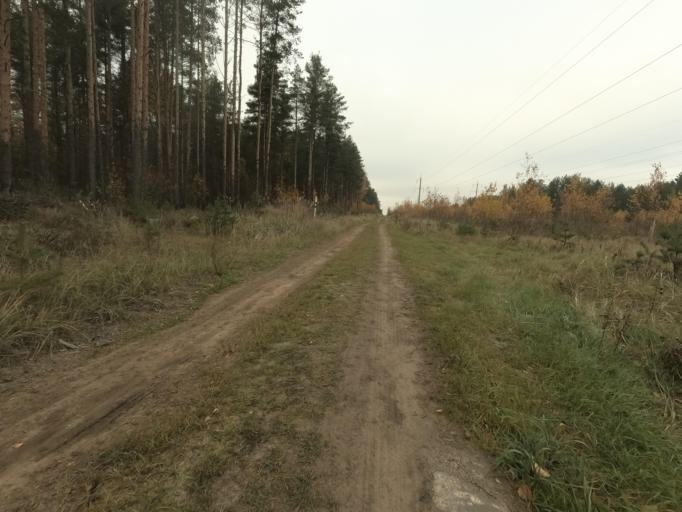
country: RU
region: Leningrad
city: Kirovsk
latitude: 59.8496
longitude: 30.9830
